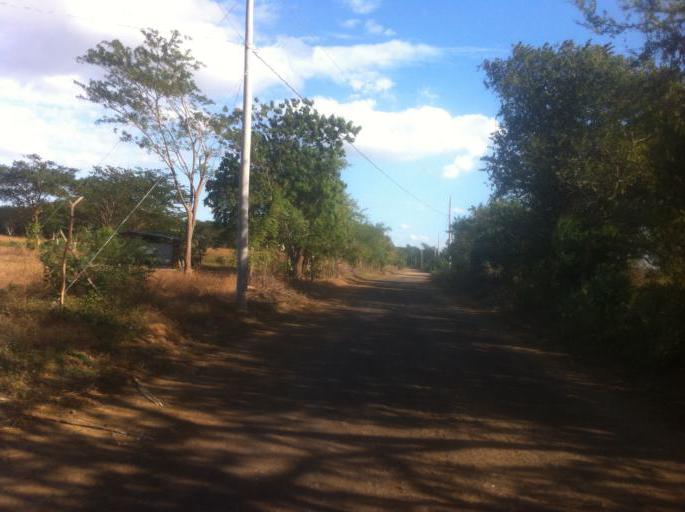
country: NI
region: Managua
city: Masachapa
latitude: 11.8791
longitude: -86.5751
